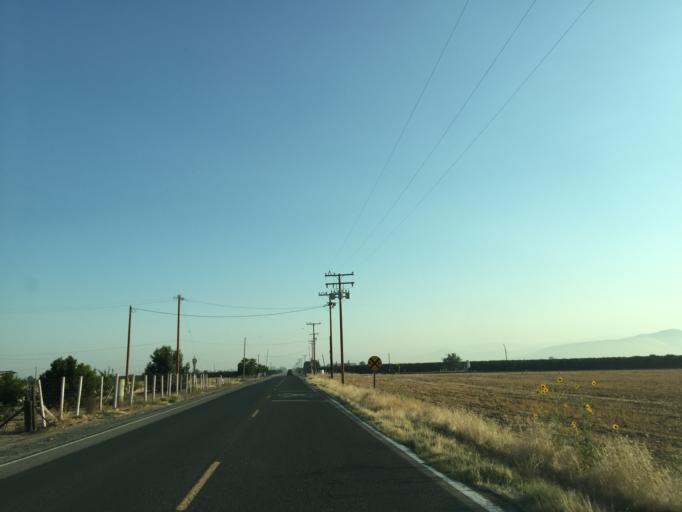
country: US
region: California
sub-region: Tulare County
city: Ivanhoe
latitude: 36.4374
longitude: -119.2778
